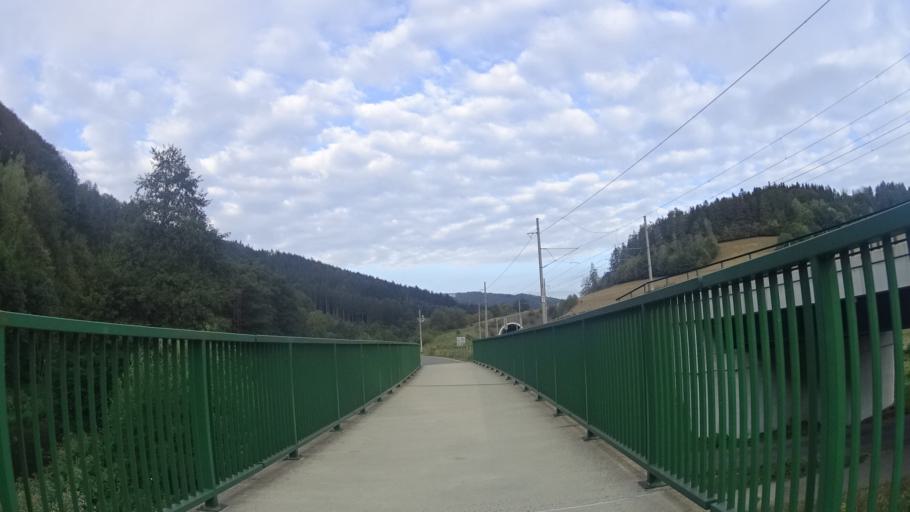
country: CZ
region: Olomoucky
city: Zabreh
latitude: 49.8635
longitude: 16.8158
